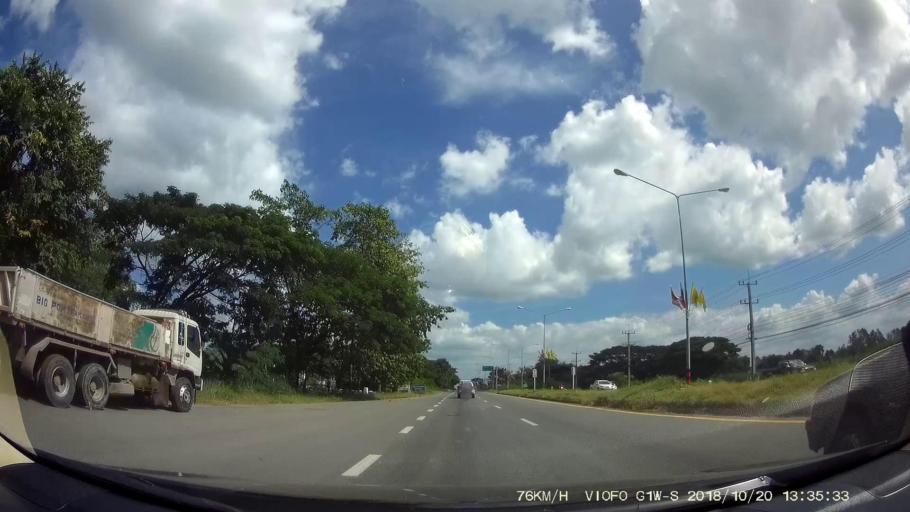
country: TH
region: Khon Kaen
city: Chum Phae
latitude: 16.5680
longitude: 102.0478
